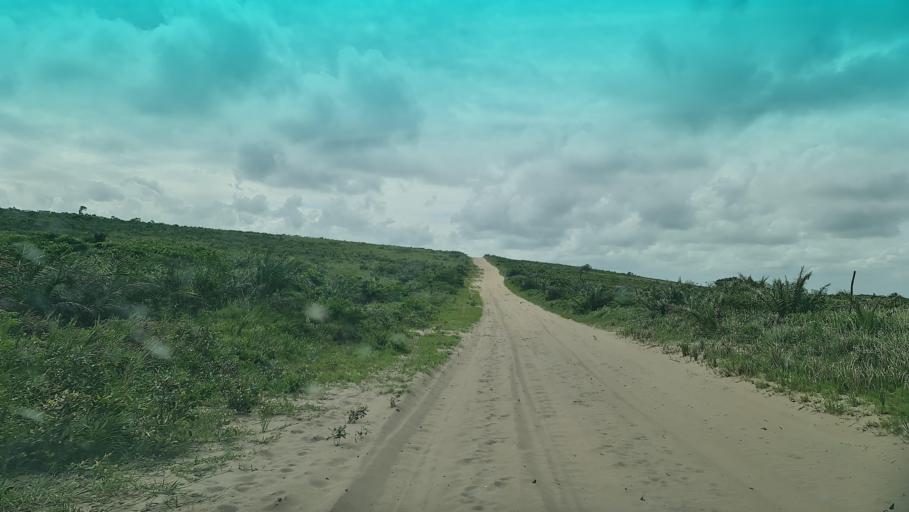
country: MZ
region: Maputo
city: Manhica
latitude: -25.4462
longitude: 32.9498
